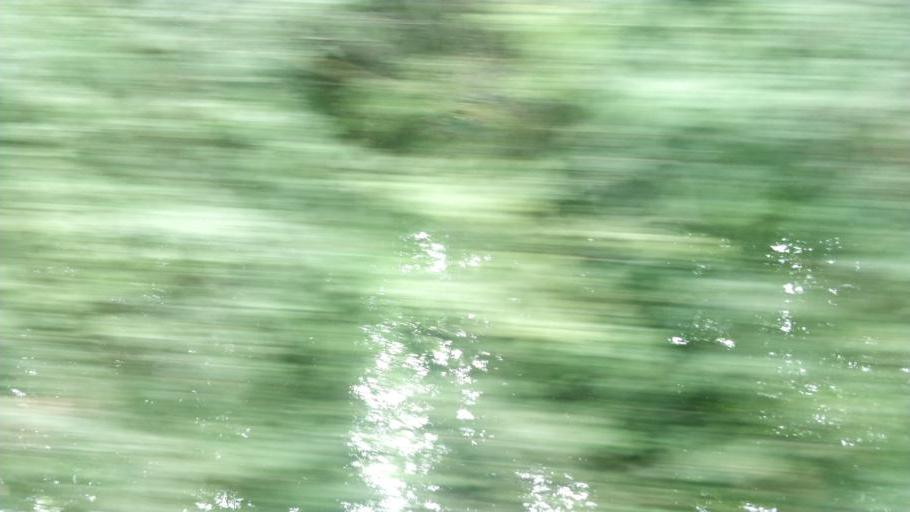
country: GB
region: Wales
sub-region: Wrexham
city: Rossett
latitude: 53.1503
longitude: -2.9358
